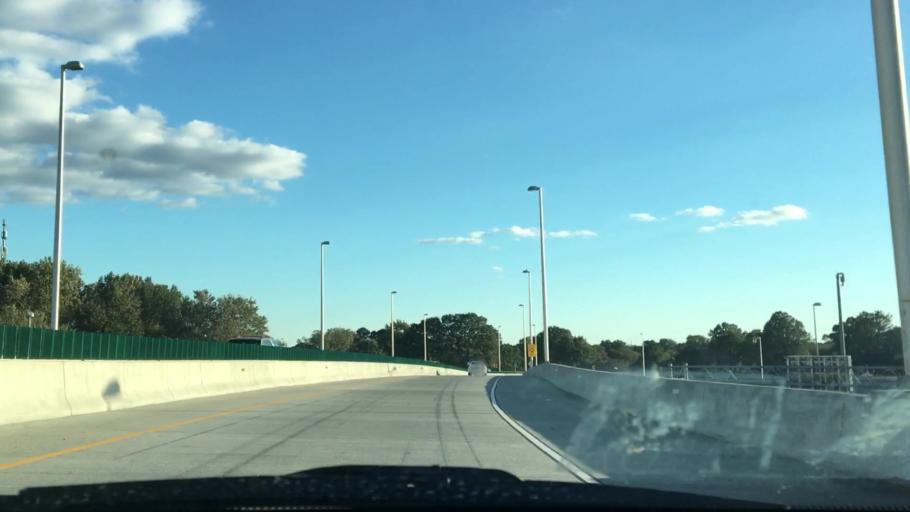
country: US
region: Virginia
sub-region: City of Portsmouth
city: Portsmouth
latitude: 36.8269
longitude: -76.3256
